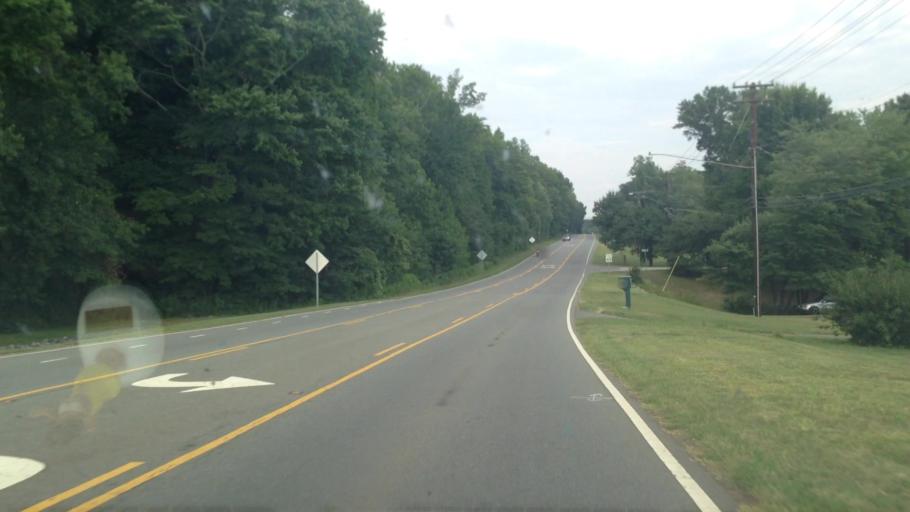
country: US
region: North Carolina
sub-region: Forsyth County
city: Kernersville
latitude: 36.1345
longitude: -80.0946
